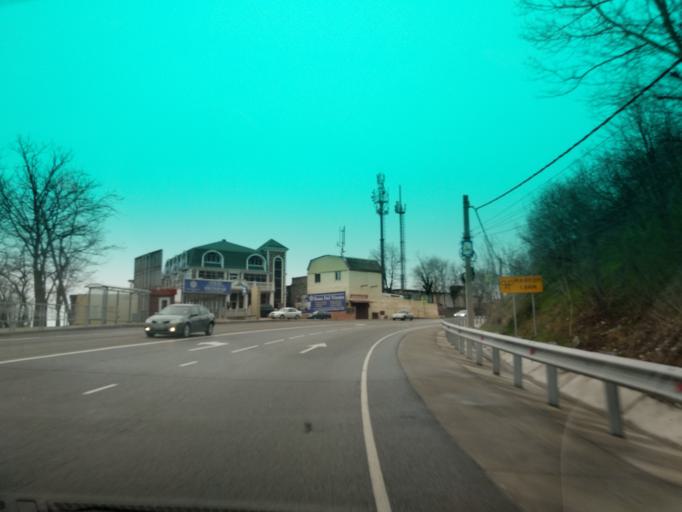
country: RU
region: Krasnodarskiy
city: Tuapse
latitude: 44.1056
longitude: 39.0773
